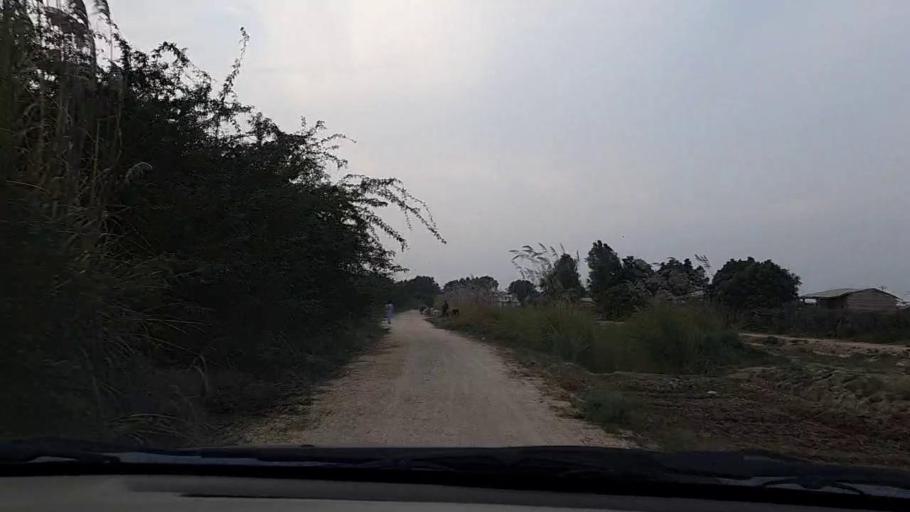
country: PK
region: Sindh
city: Thatta
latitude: 24.7706
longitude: 67.9233
